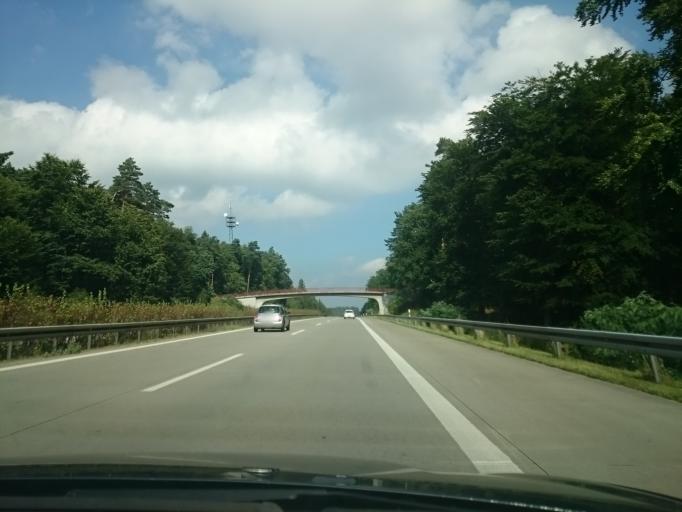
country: DE
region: Brandenburg
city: Bernau bei Berlin
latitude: 52.7424
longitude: 13.5415
